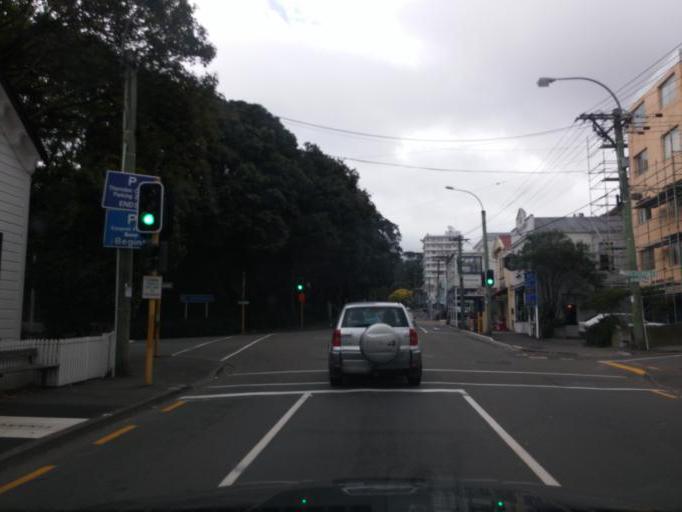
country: NZ
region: Wellington
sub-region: Wellington City
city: Kelburn
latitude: -41.2786
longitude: 174.7694
